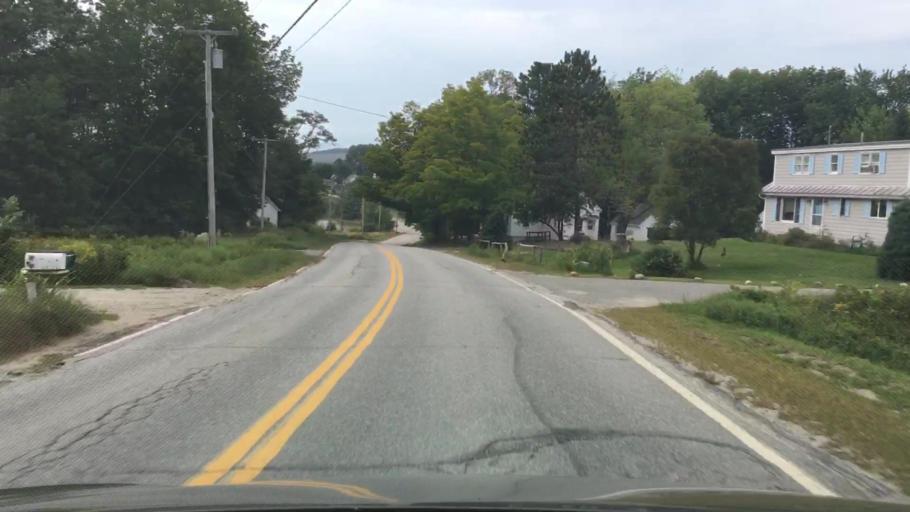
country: US
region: Maine
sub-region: Hancock County
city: Penobscot
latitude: 44.4608
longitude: -68.7060
